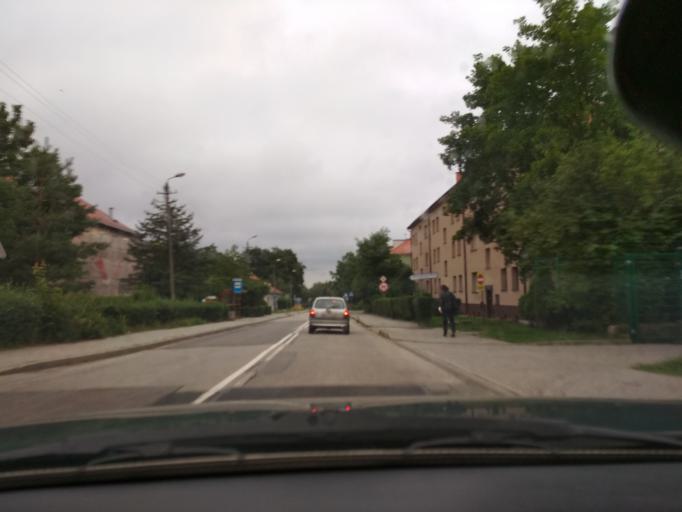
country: PL
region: Silesian Voivodeship
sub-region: Gliwice
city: Gliwice
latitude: 50.2765
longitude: 18.6709
